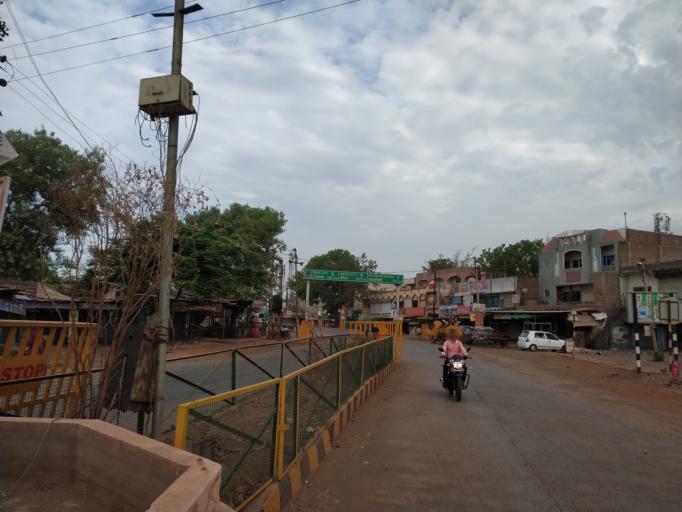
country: IN
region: Madhya Pradesh
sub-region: Shajapur
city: Agar
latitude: 23.7166
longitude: 76.0087
